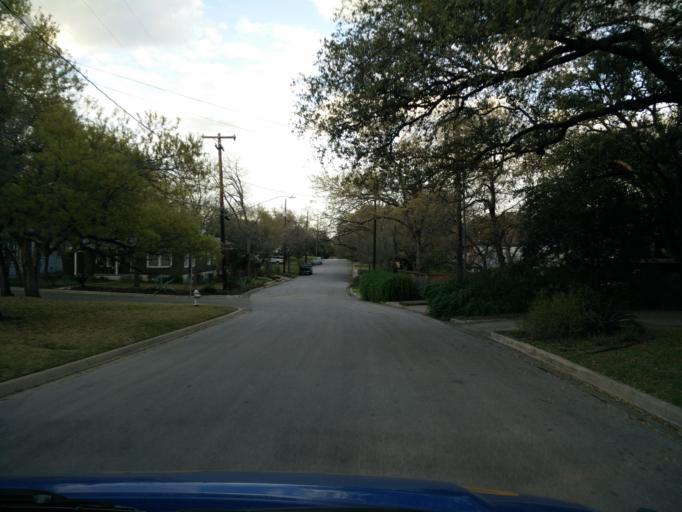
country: US
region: Texas
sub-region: Travis County
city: Austin
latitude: 30.2428
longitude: -97.7390
